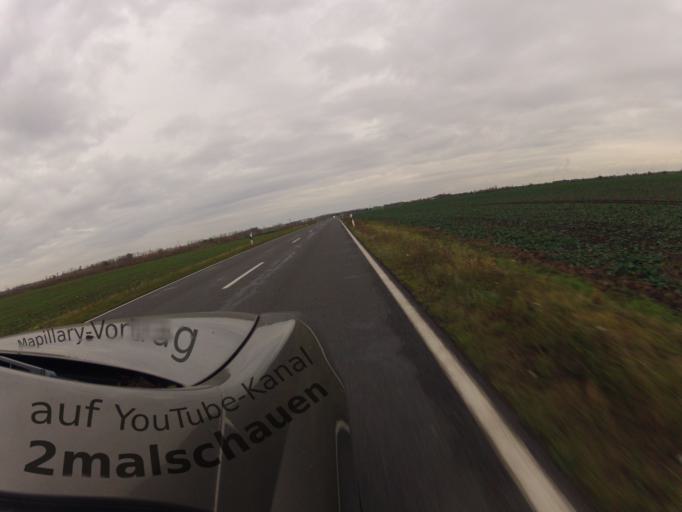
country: DE
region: Saxony-Anhalt
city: Peissen
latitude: 51.7243
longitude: 11.7341
